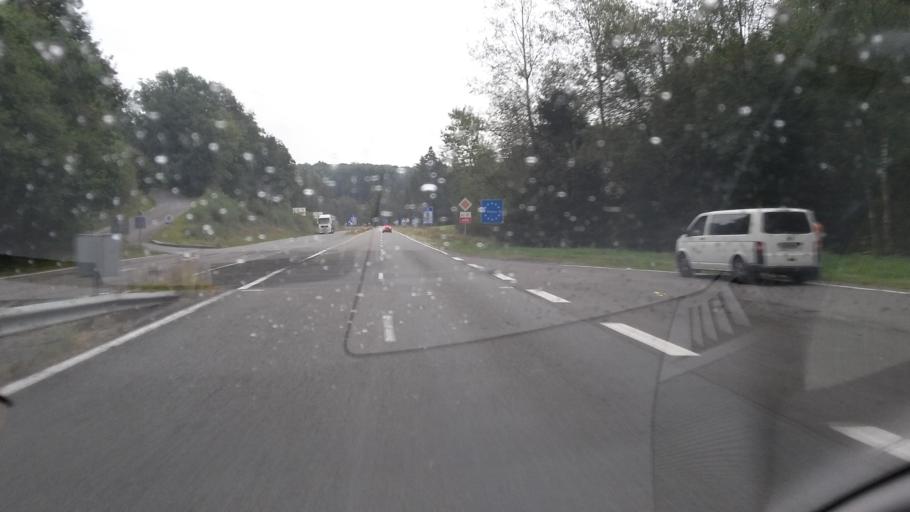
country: BE
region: Wallonia
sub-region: Province du Luxembourg
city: Bouillon
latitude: 49.7623
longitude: 5.0625
